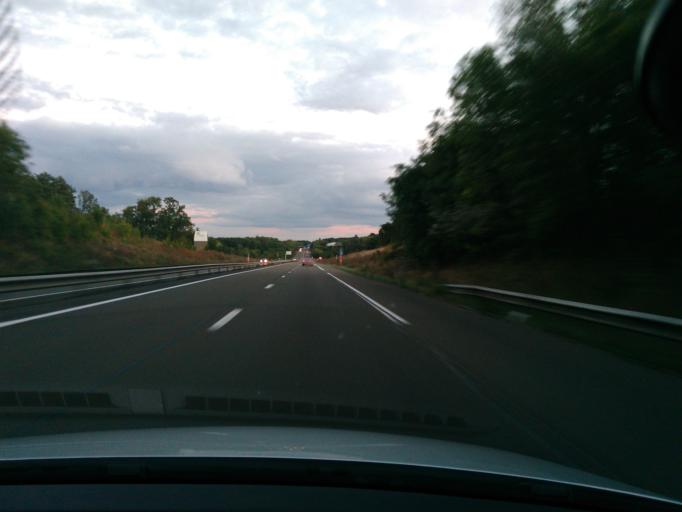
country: FR
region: Ile-de-France
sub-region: Departement de Seine-et-Marne
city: Quincy-Voisins
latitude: 48.9066
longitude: 2.8857
